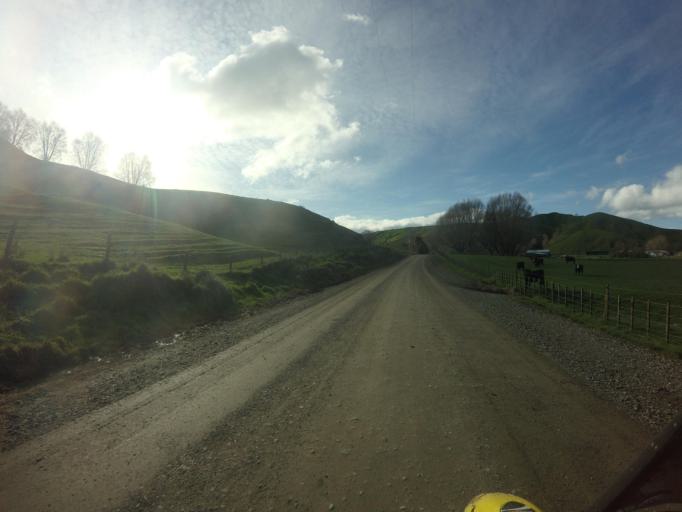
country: NZ
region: Hawke's Bay
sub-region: Wairoa District
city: Wairoa
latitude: -38.9918
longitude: 177.5925
